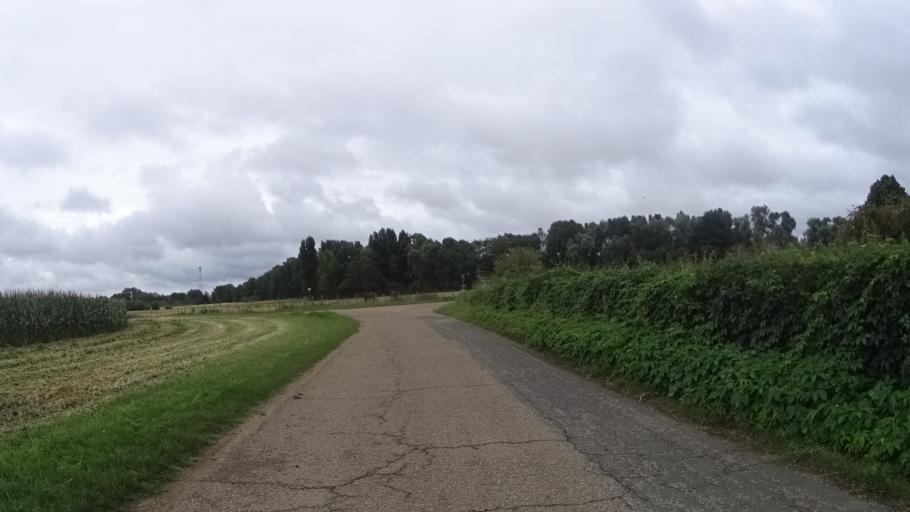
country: FR
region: Centre
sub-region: Departement du Loir-et-Cher
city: Montlivault
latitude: 47.6563
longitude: 1.4475
